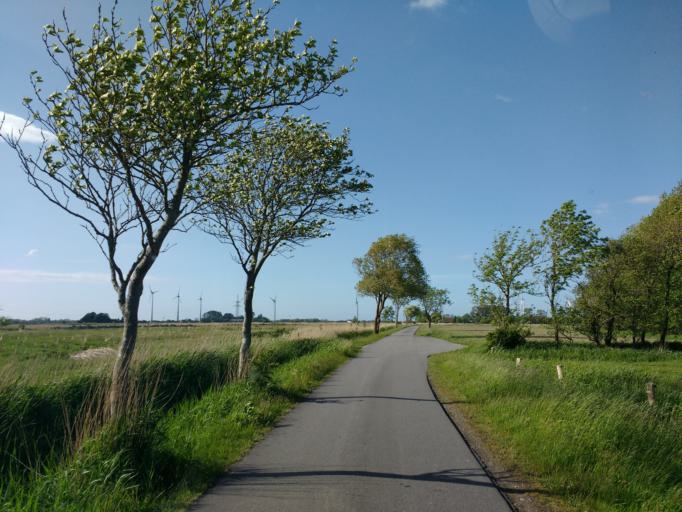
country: DE
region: Lower Saxony
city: Schillig
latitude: 53.6726
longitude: 7.9298
